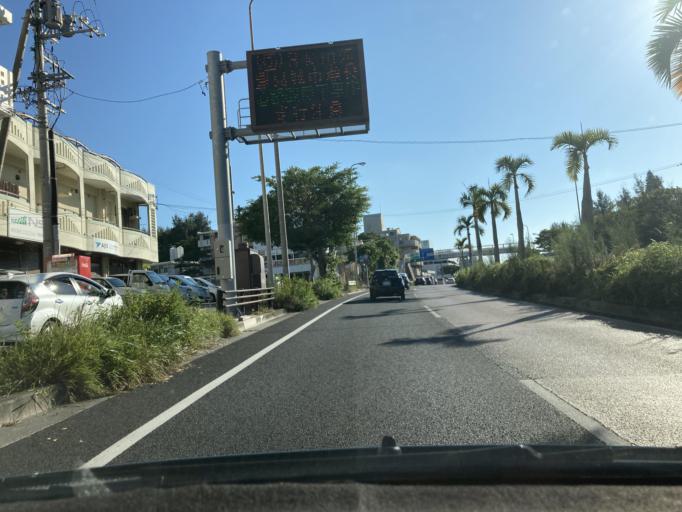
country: JP
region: Okinawa
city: Naha-shi
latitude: 26.1991
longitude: 127.6616
